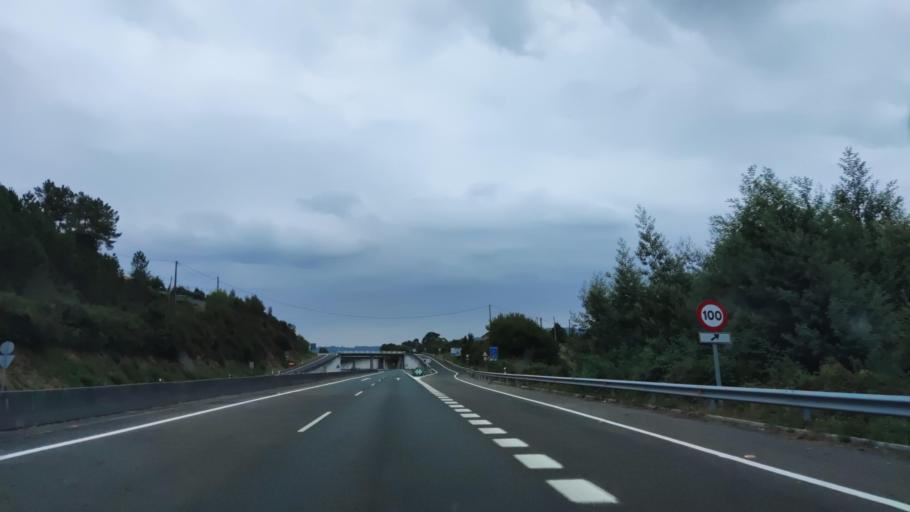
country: ES
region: Galicia
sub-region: Provincia da Coruna
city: Santiago de Compostela
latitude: 42.8229
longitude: -8.5312
